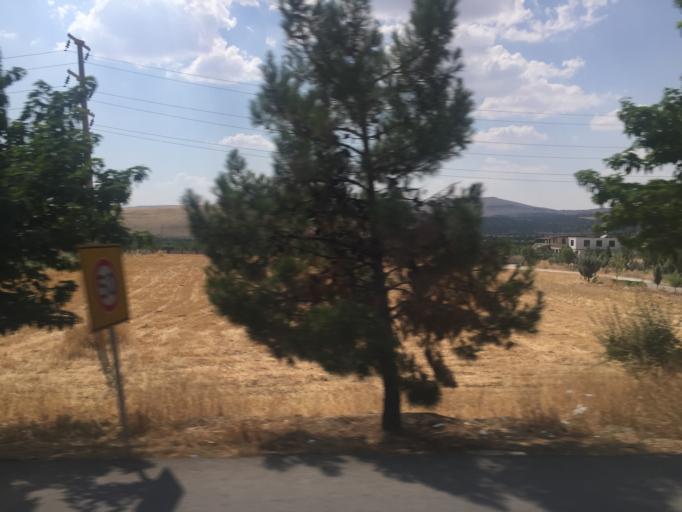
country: TR
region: Sanliurfa
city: Sanliurfa
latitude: 37.2440
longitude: 38.7936
